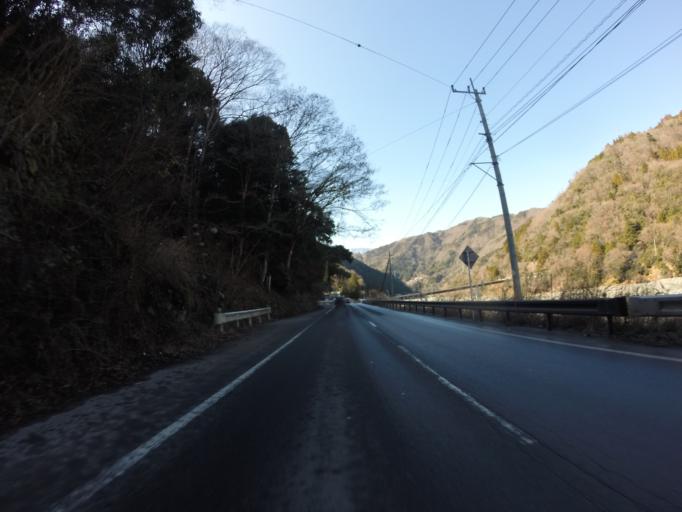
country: JP
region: Yamanashi
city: Ryuo
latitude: 35.4221
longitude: 138.3994
